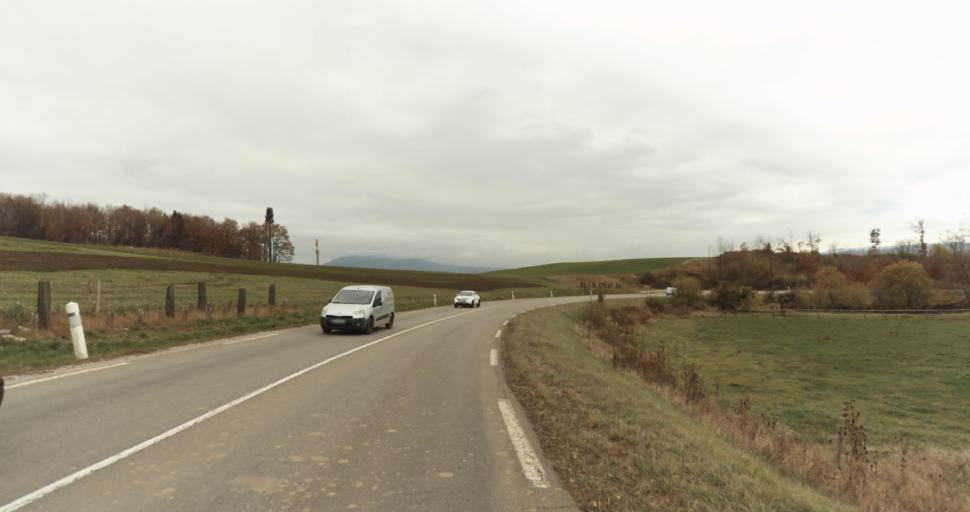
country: FR
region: Rhone-Alpes
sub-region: Departement de la Haute-Savoie
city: Pringy
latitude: 45.9554
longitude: 6.1270
